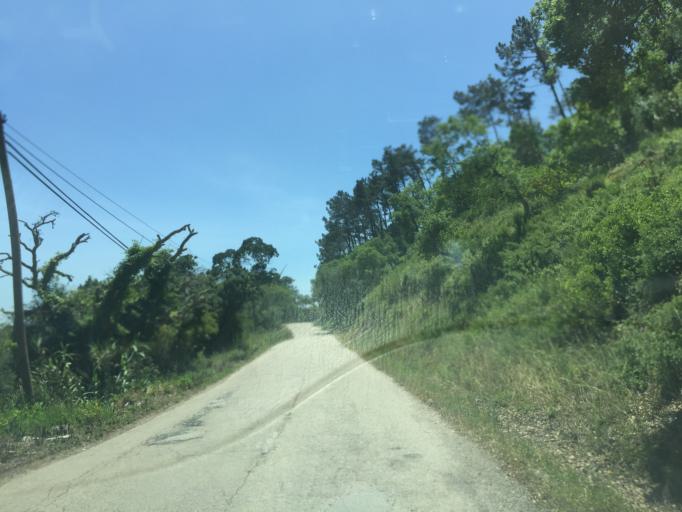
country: PT
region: Lisbon
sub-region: Mafra
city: Venda do Pinheiro
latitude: 38.8908
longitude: -9.2271
